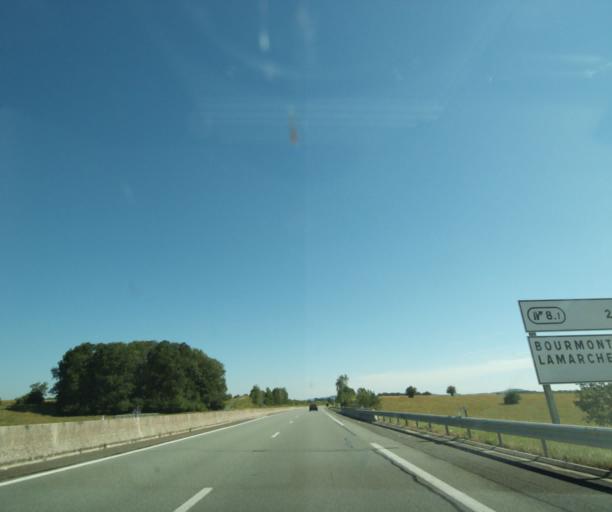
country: FR
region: Champagne-Ardenne
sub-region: Departement de la Haute-Marne
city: Avrecourt
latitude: 48.0052
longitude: 5.5171
